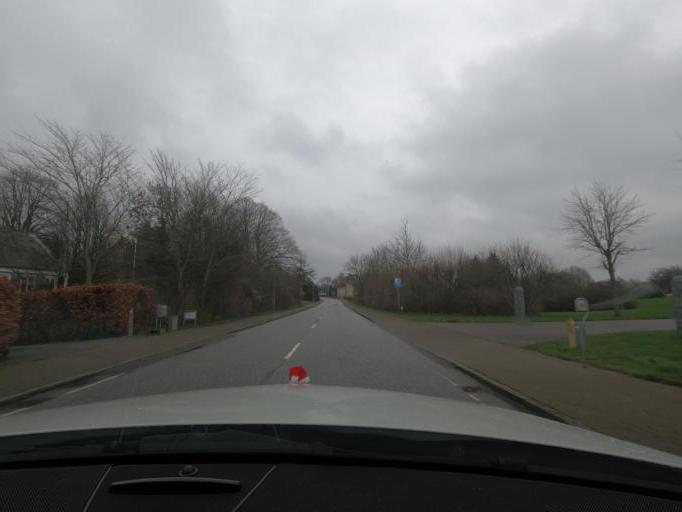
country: DK
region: South Denmark
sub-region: Haderslev Kommune
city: Starup
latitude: 55.2543
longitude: 9.6732
